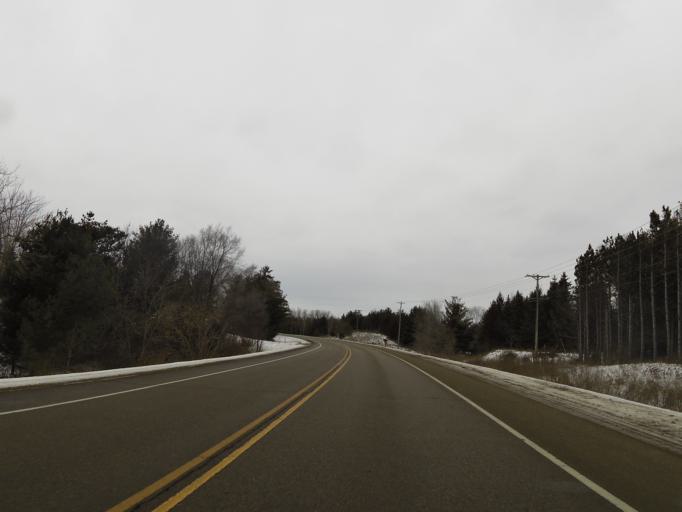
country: US
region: Minnesota
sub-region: Washington County
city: Bayport
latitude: 45.0385
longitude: -92.7542
